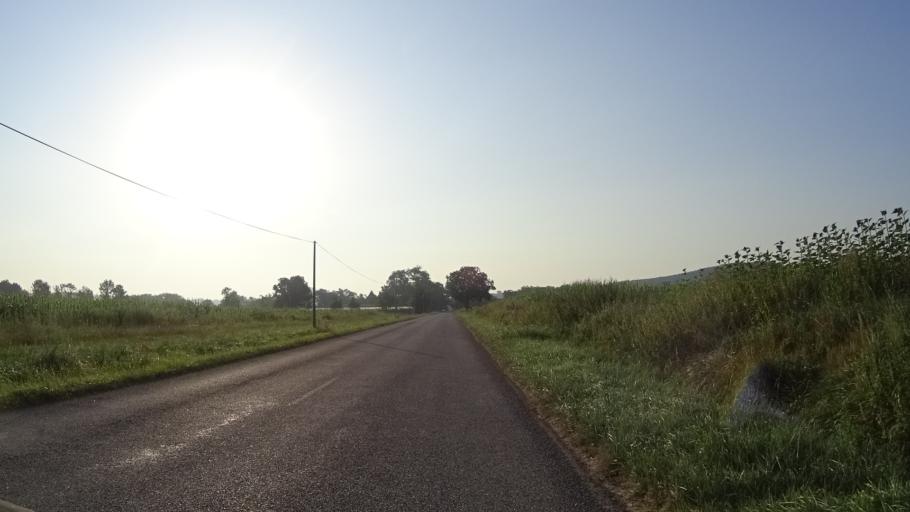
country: FR
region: Midi-Pyrenees
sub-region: Departement de l'Ariege
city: Mirepoix
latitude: 43.0852
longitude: 1.8935
